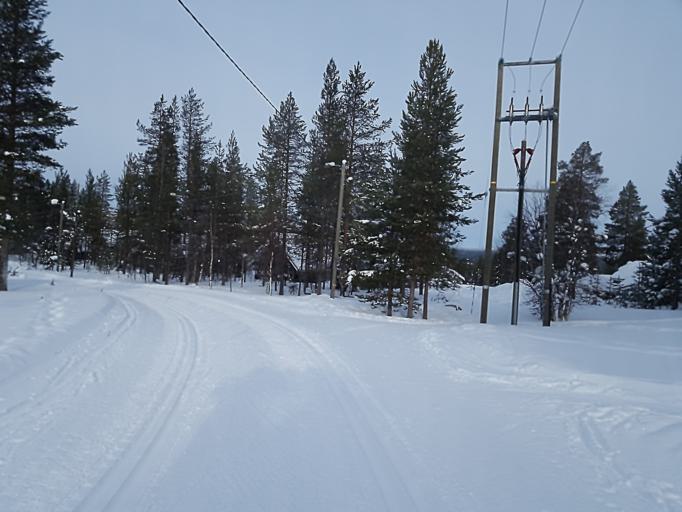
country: FI
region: Lapland
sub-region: Tunturi-Lappi
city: Kolari
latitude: 67.5965
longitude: 24.1584
